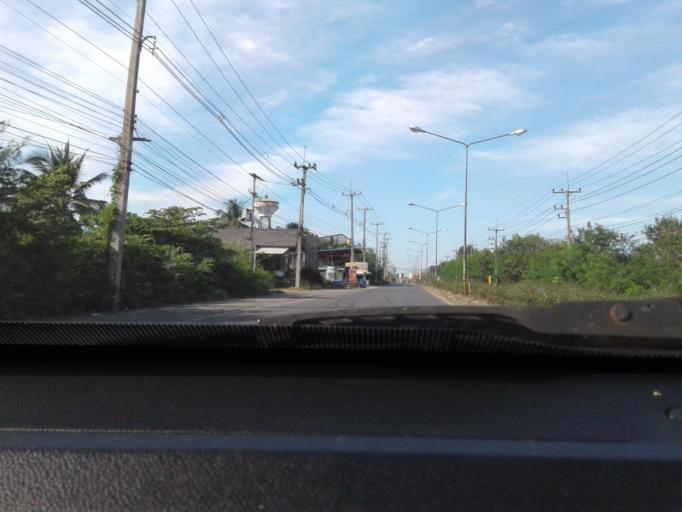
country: TH
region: Nakhon Pathom
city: Salaya
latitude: 13.8682
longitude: 100.2947
